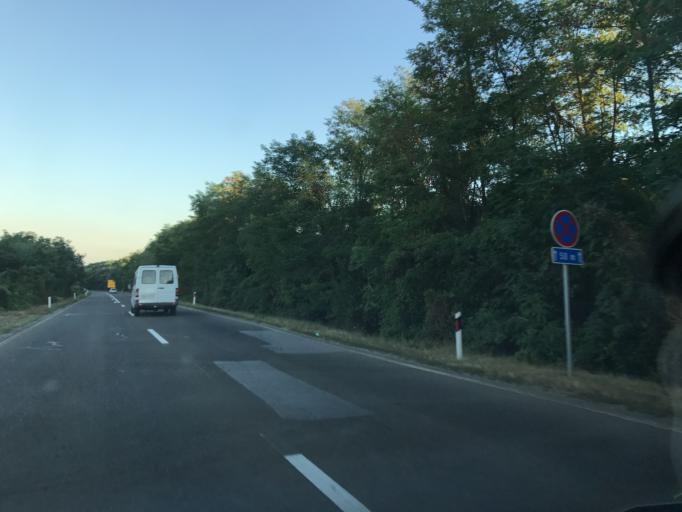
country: RS
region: Central Serbia
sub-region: Branicevski Okrug
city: Pozarevac
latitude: 44.6504
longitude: 21.2059
